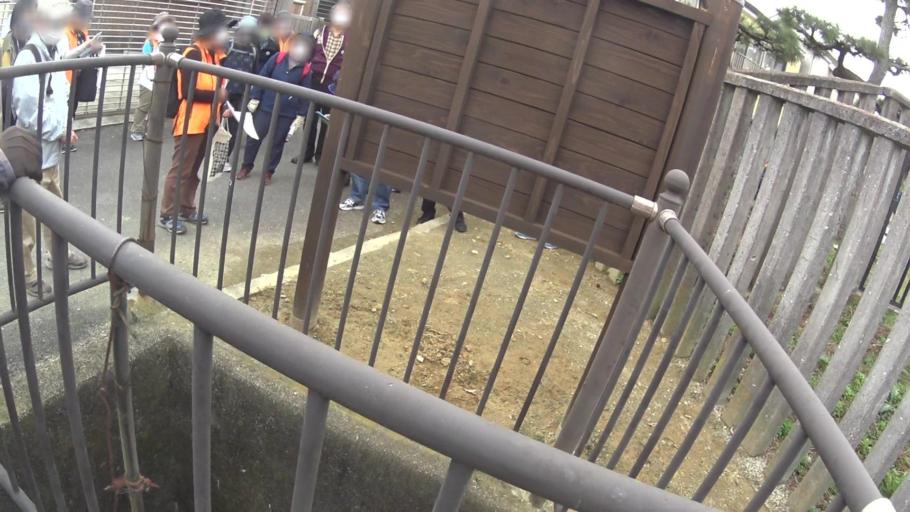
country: JP
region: Osaka
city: Kashihara
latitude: 34.5636
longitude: 135.5949
